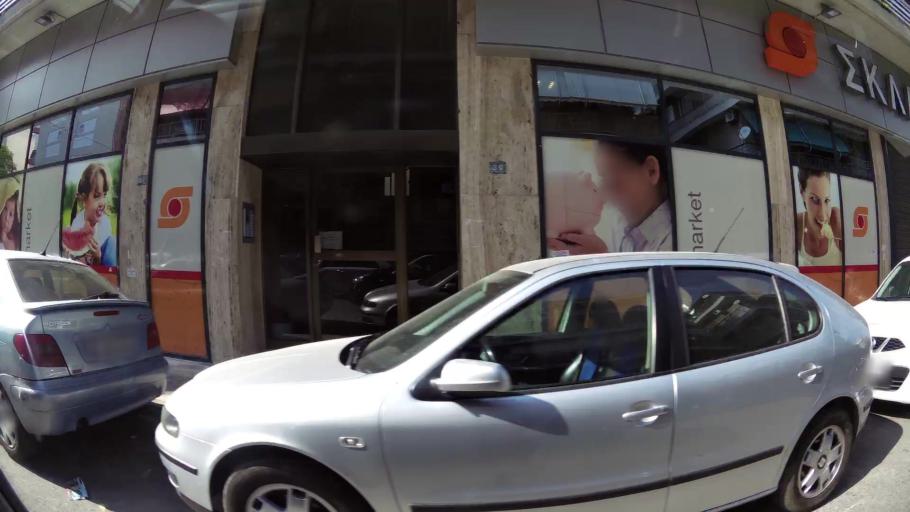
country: GR
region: Attica
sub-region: Nomarchia Athinas
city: Athens
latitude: 37.9949
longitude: 23.7177
